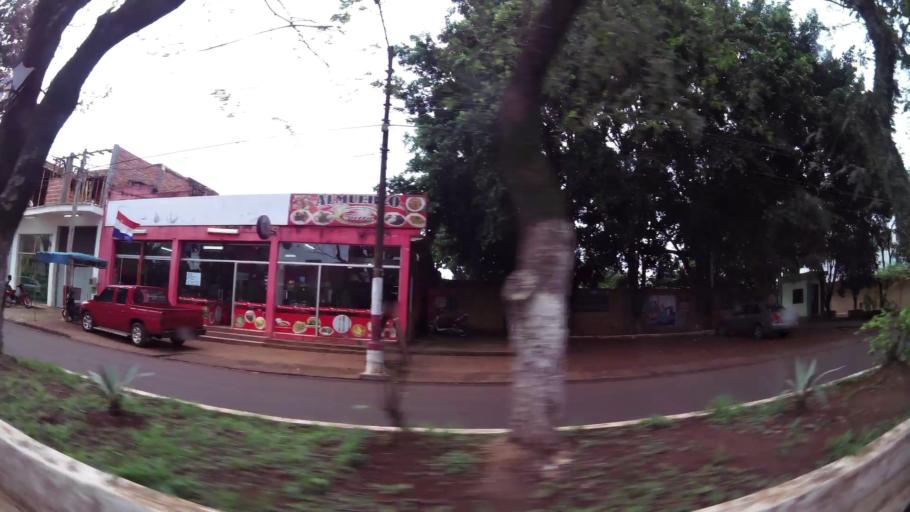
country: PY
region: Alto Parana
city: Ciudad del Este
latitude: -25.4072
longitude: -54.6325
